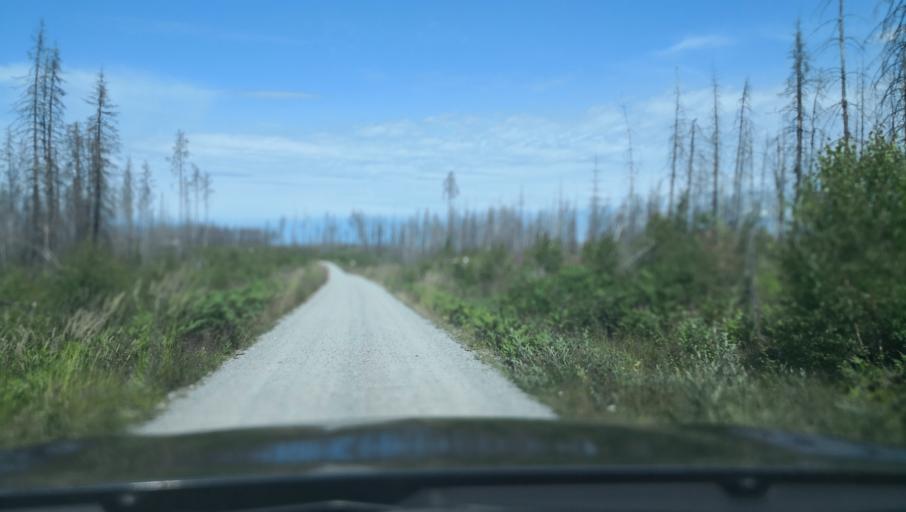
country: SE
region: Vaestmanland
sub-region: Surahammars Kommun
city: Ramnas
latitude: 59.9081
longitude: 16.1478
